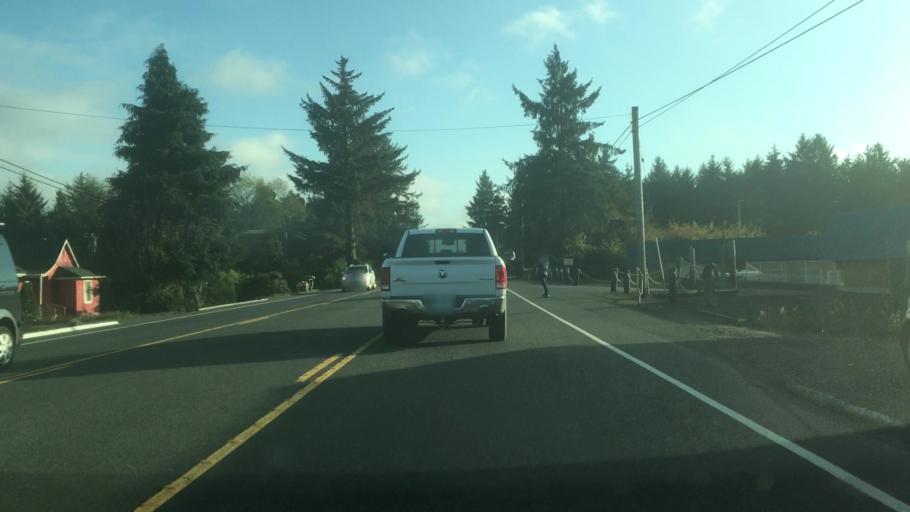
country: US
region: Oregon
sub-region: Clatsop County
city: Gearhart
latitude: 46.0186
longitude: -123.9115
